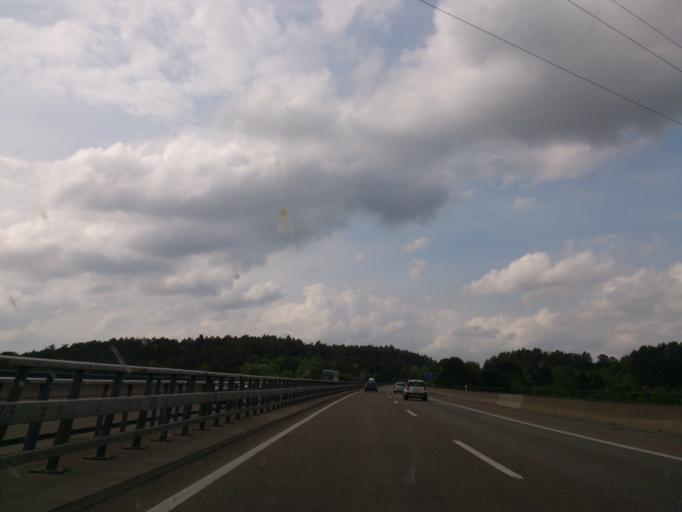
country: DE
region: Hesse
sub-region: Regierungsbezirk Kassel
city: Breuna
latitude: 51.4122
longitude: 9.1637
